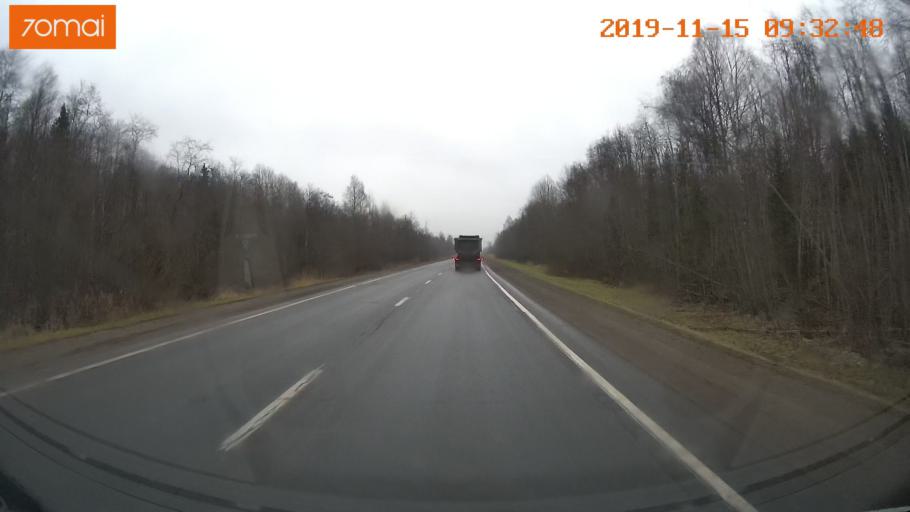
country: RU
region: Vologda
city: Sheksna
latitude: 59.2700
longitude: 38.3439
